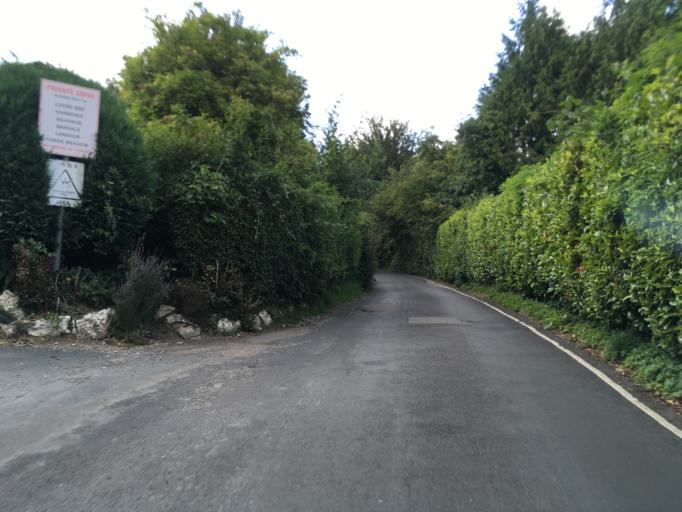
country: GB
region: England
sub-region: Kent
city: Maidstone
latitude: 51.2415
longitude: 0.5139
